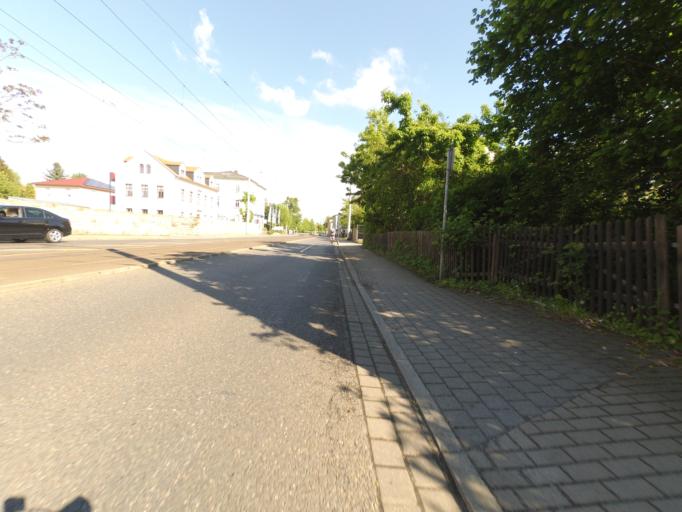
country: DE
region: Saxony
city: Albertstadt
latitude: 51.0264
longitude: 13.8030
